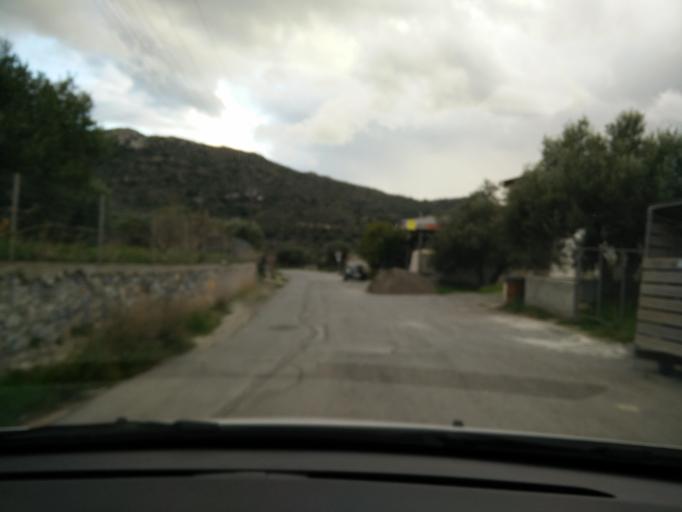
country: GR
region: Crete
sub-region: Nomos Lasithiou
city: Kritsa
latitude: 35.0934
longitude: 25.6868
